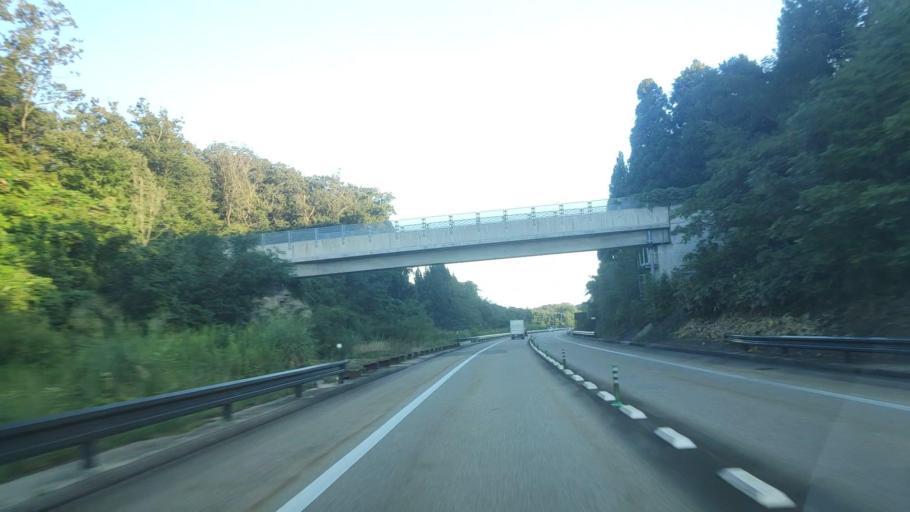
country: JP
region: Ishikawa
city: Nanao
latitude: 37.0038
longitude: 137.0404
